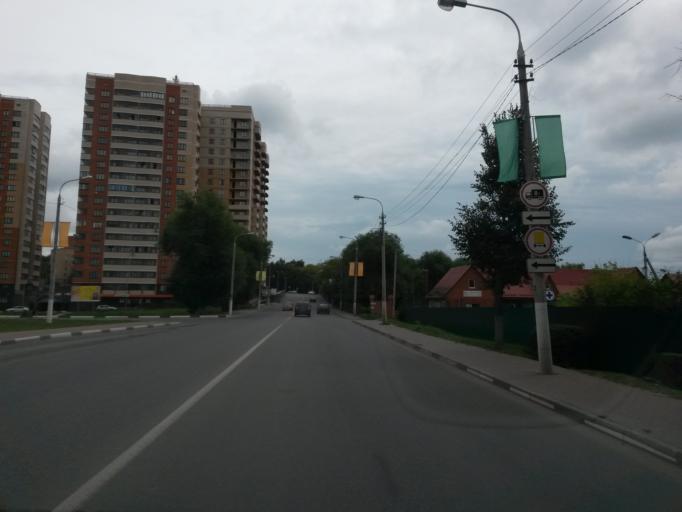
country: RU
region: Moskovskaya
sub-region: Chekhovskiy Rayon
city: Chekhov
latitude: 55.1421
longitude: 37.4543
